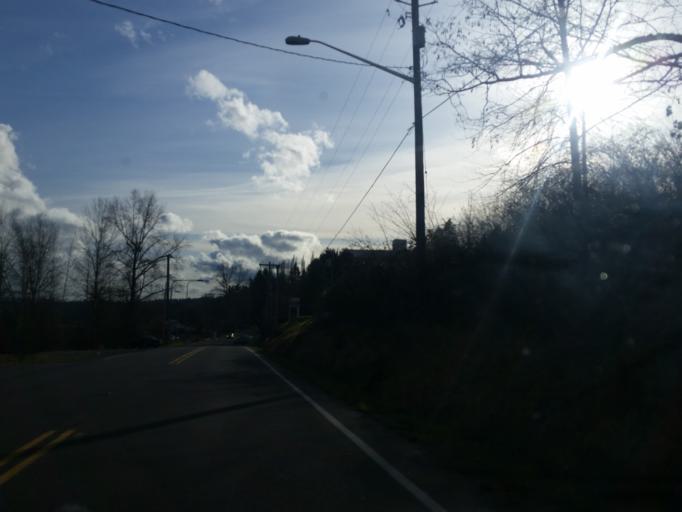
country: US
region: Washington
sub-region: King County
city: Kingsgate
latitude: 47.7137
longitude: -122.1539
